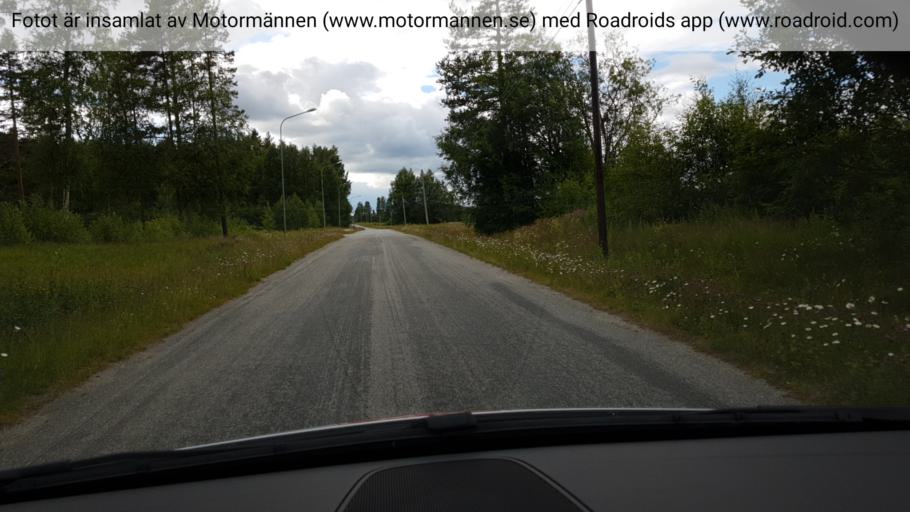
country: SE
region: Vaesterbotten
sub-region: Dorotea Kommun
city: Dorotea
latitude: 63.9129
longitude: 16.3100
